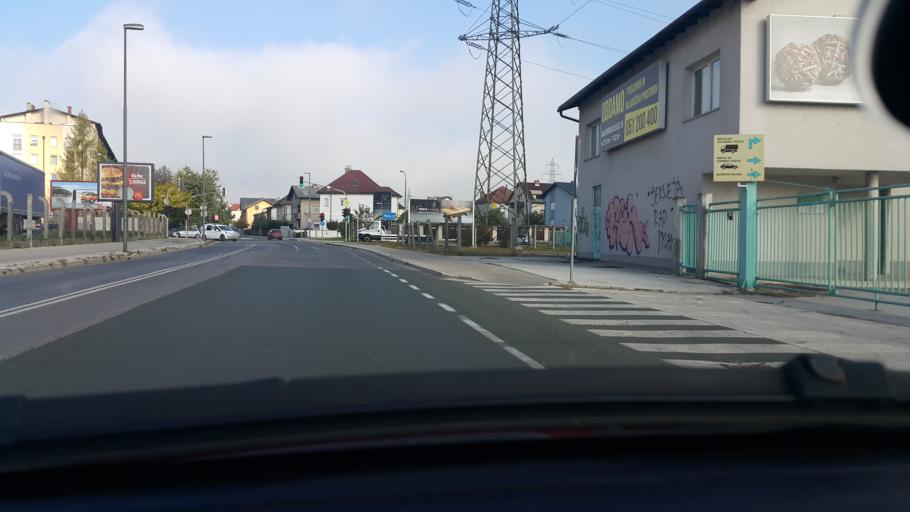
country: SI
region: Ljubljana
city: Ljubljana
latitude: 46.0635
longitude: 14.5375
